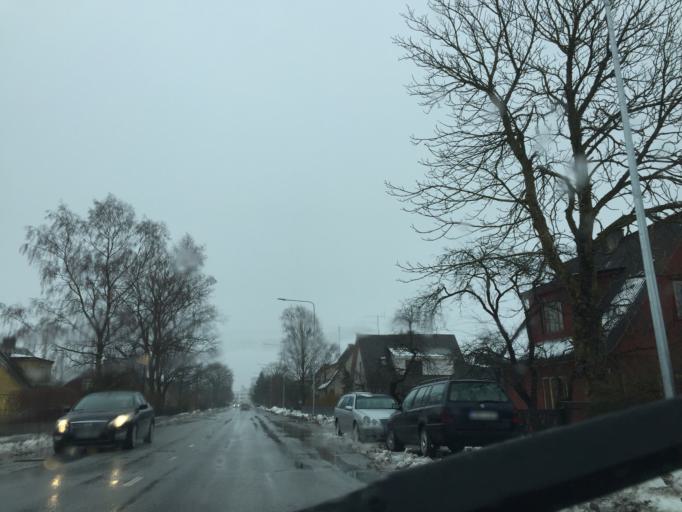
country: EE
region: Saare
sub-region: Kuressaare linn
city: Kuressaare
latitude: 58.2603
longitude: 22.4924
